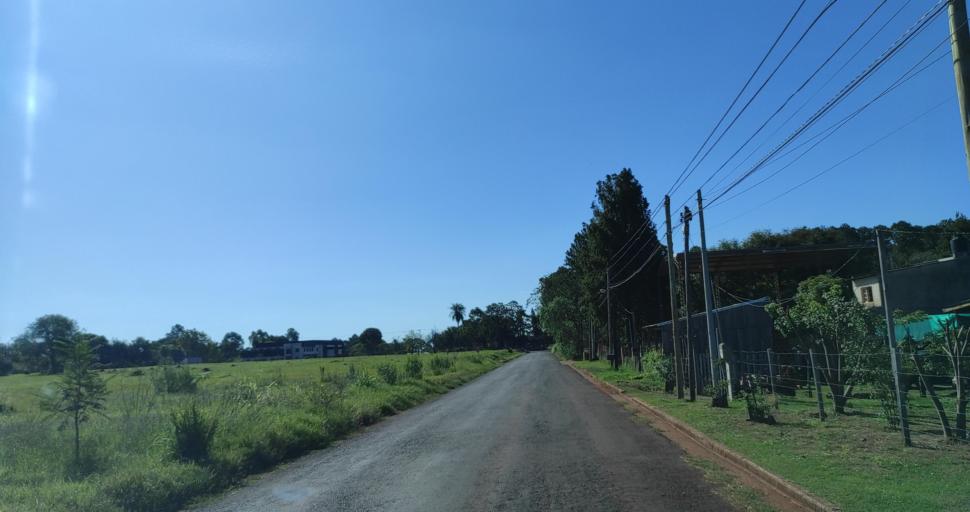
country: AR
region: Misiones
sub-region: Departamento de Capital
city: Posadas
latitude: -27.4286
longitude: -55.9298
